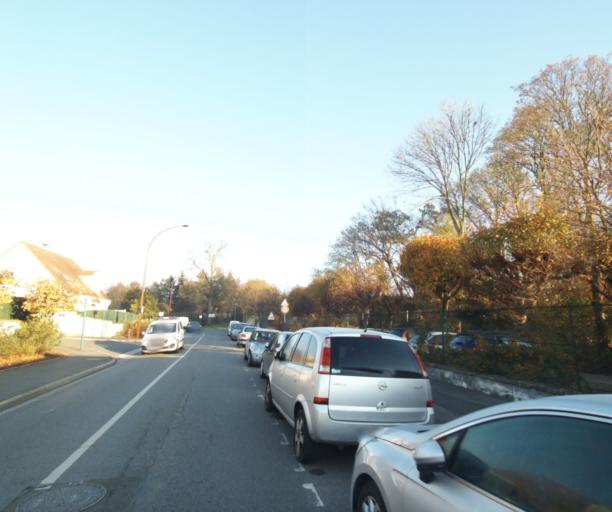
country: FR
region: Ile-de-France
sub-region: Departement du Val-d'Oise
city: Gonesse
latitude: 48.9899
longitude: 2.4464
